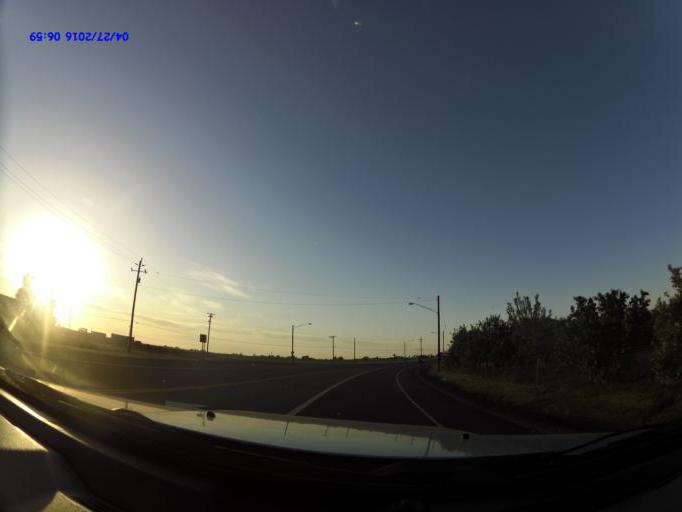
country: US
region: California
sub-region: San Joaquin County
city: Escalon
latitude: 37.8353
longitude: -120.9990
